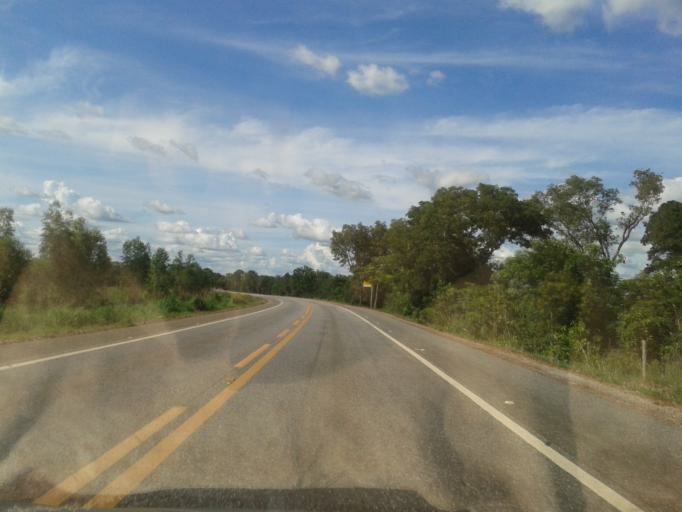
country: BR
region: Goias
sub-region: Mozarlandia
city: Mozarlandia
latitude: -14.8968
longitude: -50.5487
